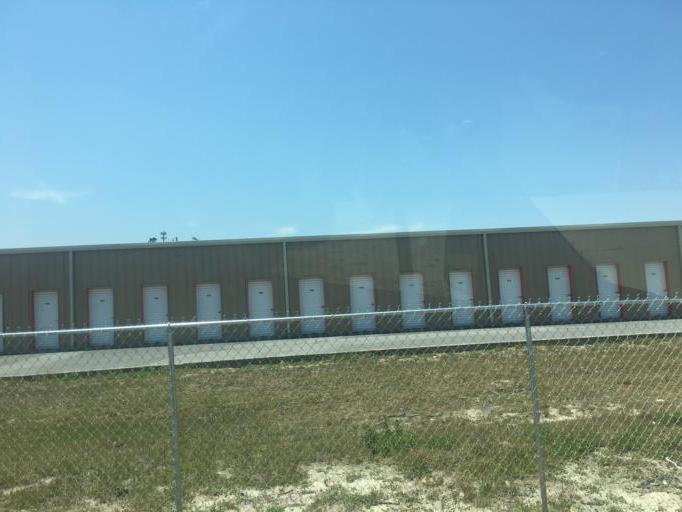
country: US
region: Florida
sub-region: Bay County
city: Hiland Park
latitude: 30.2132
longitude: -85.6521
